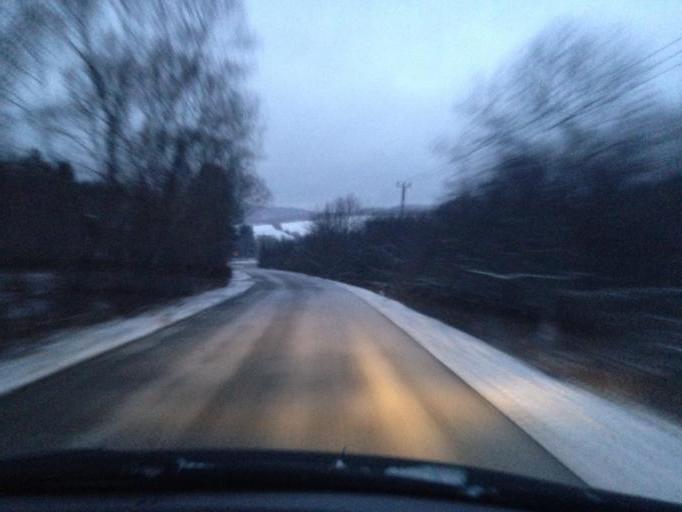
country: PL
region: Subcarpathian Voivodeship
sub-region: Powiat jasielski
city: Krempna
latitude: 49.5220
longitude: 21.5480
